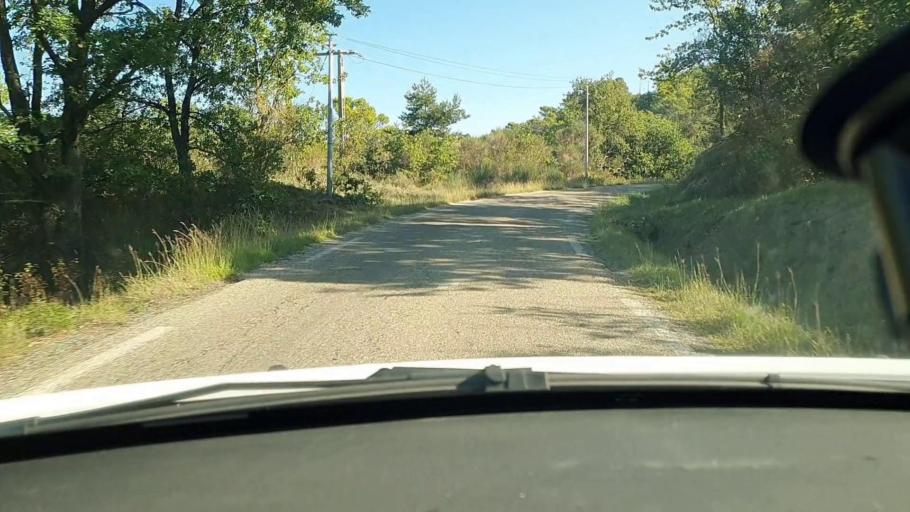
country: FR
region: Languedoc-Roussillon
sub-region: Departement du Gard
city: Saint-Julien-de-Peyrolas
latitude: 44.2554
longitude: 4.5216
